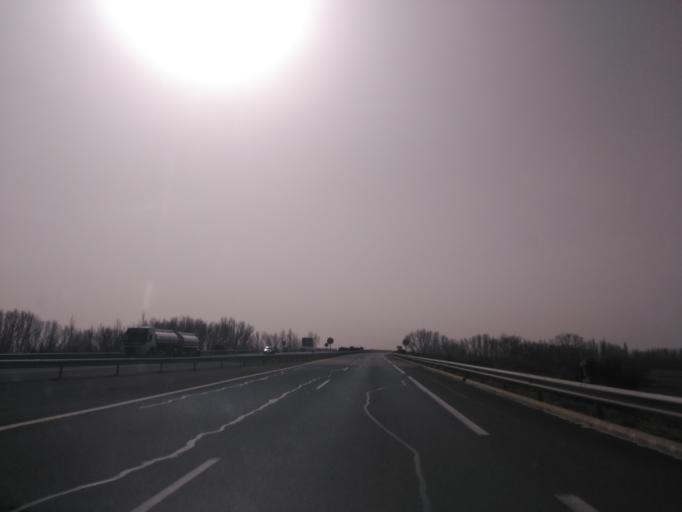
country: ES
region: Castille and Leon
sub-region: Provincia de Palencia
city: Fromista
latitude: 42.2526
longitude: -4.4181
